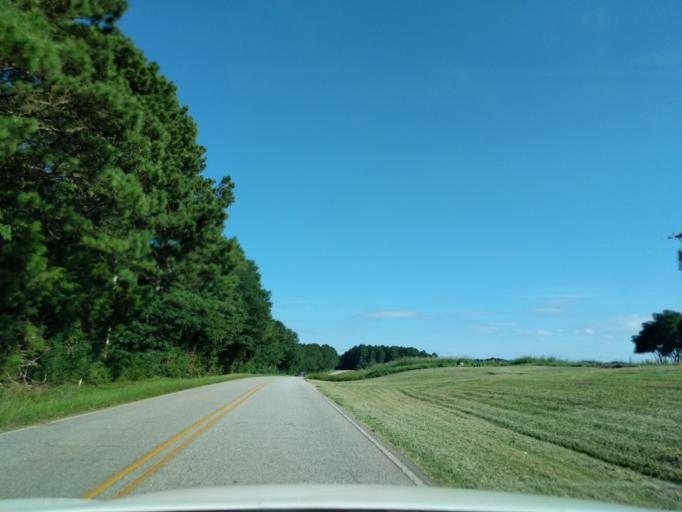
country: US
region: Georgia
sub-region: Oglethorpe County
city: Lexington
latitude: 33.9233
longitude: -83.0298
